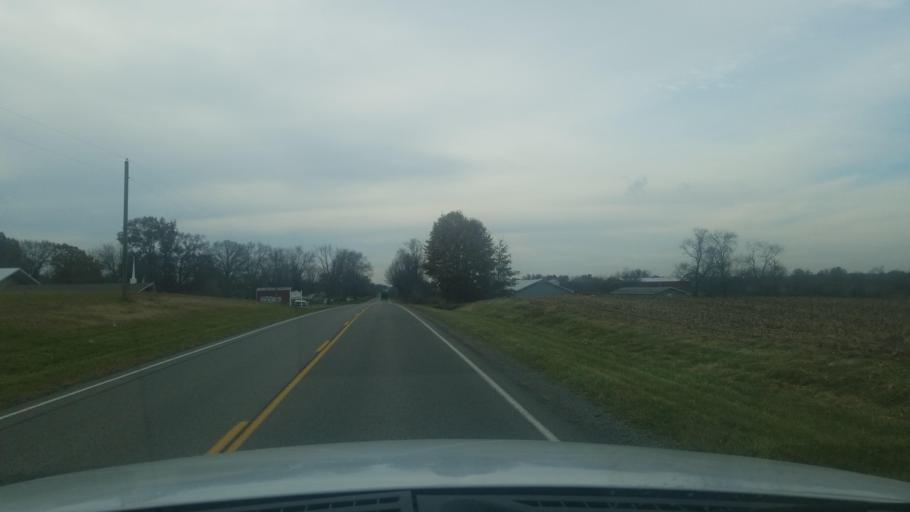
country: US
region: Illinois
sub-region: Saline County
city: Carrier Mills
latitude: 37.7991
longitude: -88.6517
